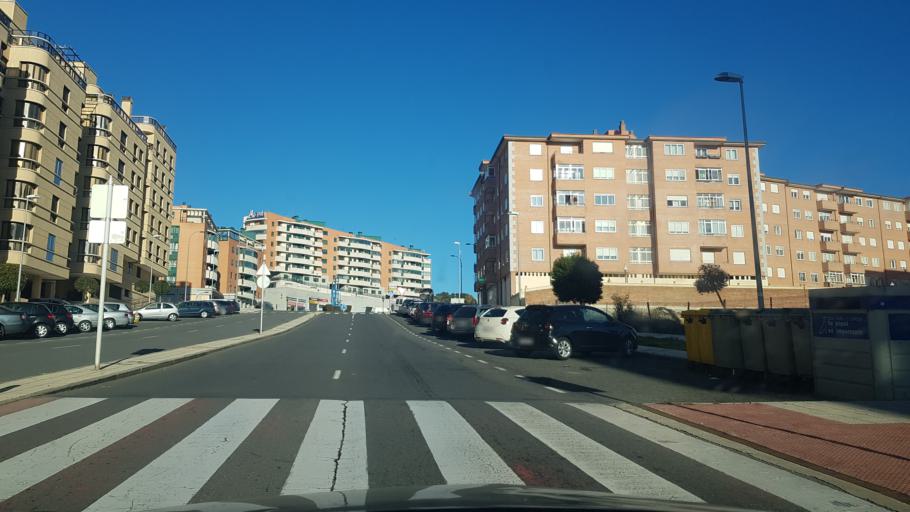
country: ES
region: Castille and Leon
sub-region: Provincia de Avila
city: Avila
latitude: 40.6496
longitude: -4.6764
